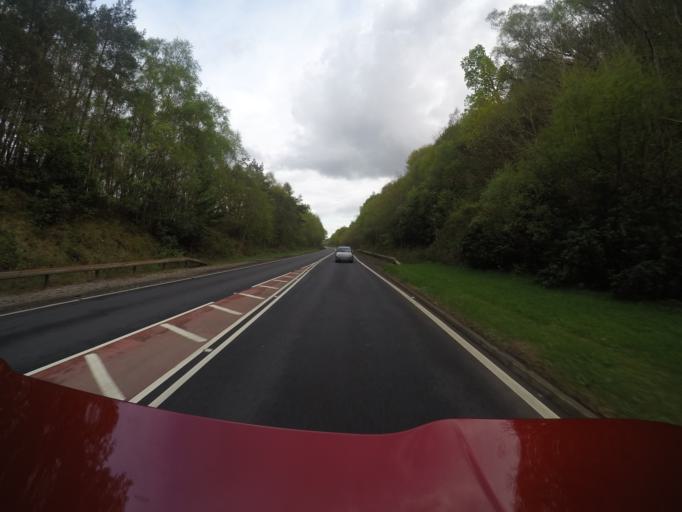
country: GB
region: Scotland
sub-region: Argyll and Bute
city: Helensburgh
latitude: 56.1438
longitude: -4.6636
